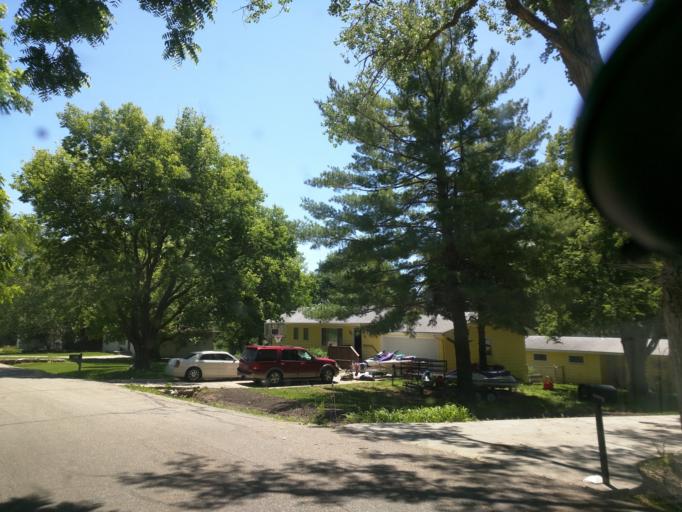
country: US
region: Kansas
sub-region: Riley County
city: Manhattan
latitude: 39.2151
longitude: -96.6160
